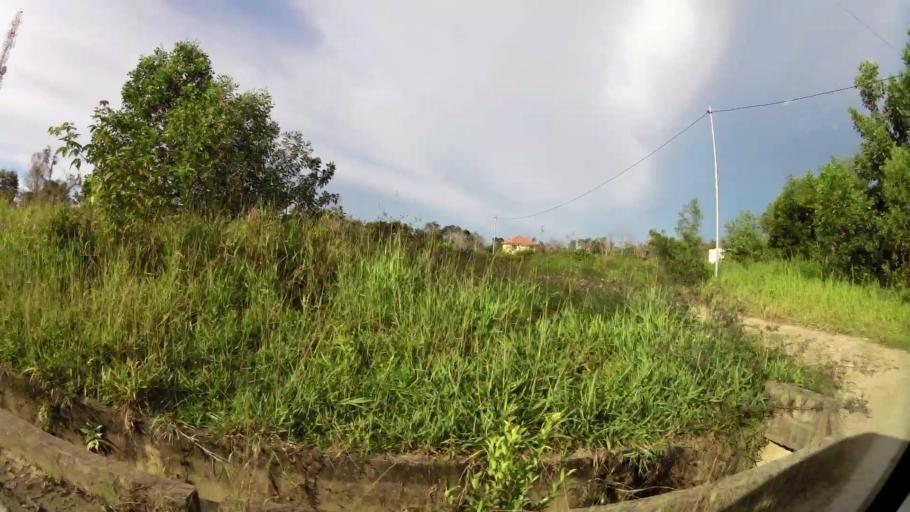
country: BN
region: Brunei and Muara
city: Bandar Seri Begawan
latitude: 4.9569
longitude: 115.0225
